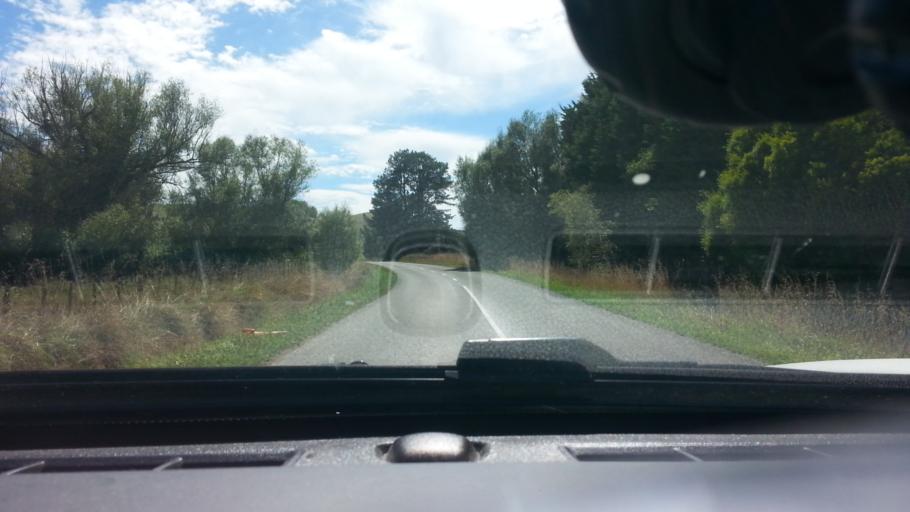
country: NZ
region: Wellington
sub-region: Masterton District
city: Masterton
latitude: -41.0680
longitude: 175.8377
